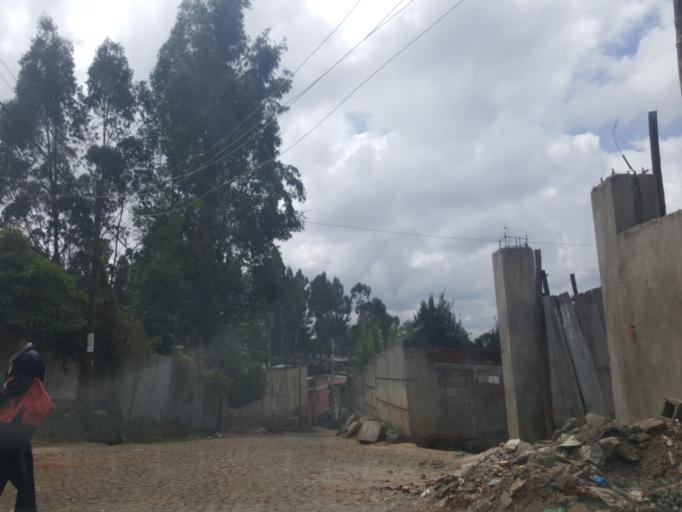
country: ET
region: Adis Abeba
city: Addis Ababa
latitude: 9.0686
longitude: 38.7384
